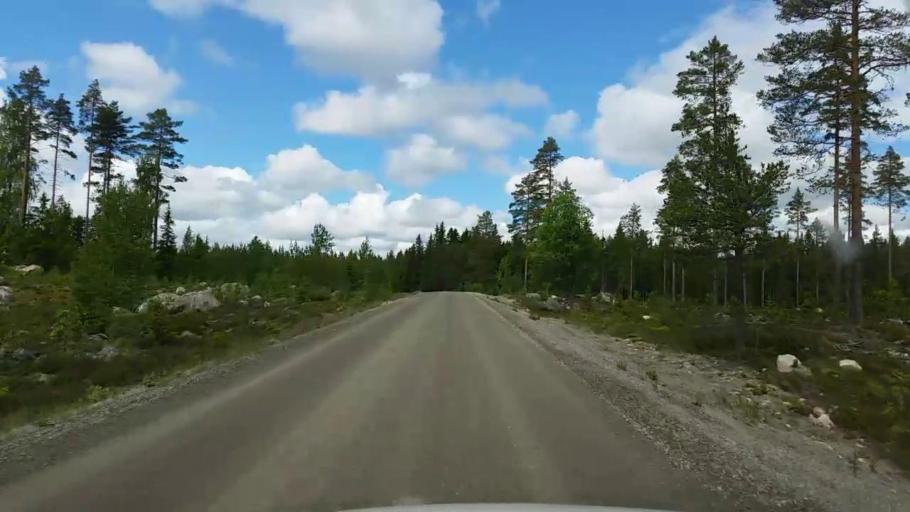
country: SE
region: Gaevleborg
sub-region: Bollnas Kommun
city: Kilafors
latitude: 61.0279
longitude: 16.3765
